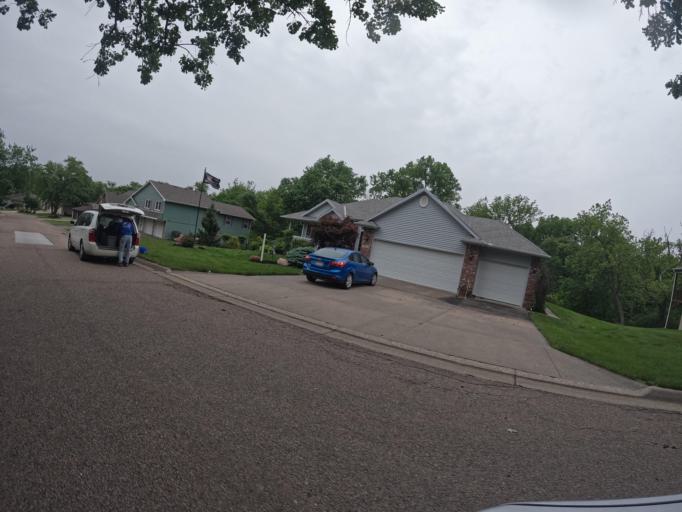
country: US
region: Nebraska
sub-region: Sarpy County
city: Offutt Air Force Base
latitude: 41.0453
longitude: -95.9738
